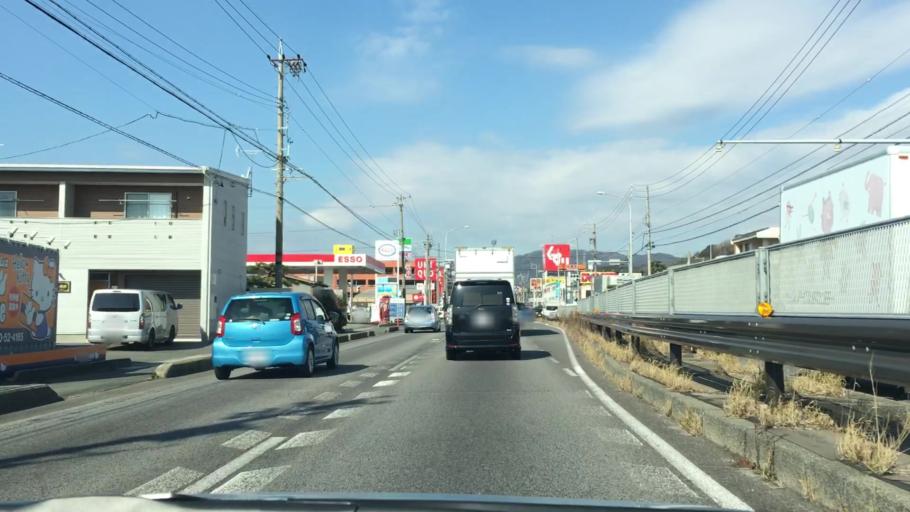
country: JP
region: Aichi
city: Kozakai-cho
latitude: 34.8423
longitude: 137.3236
